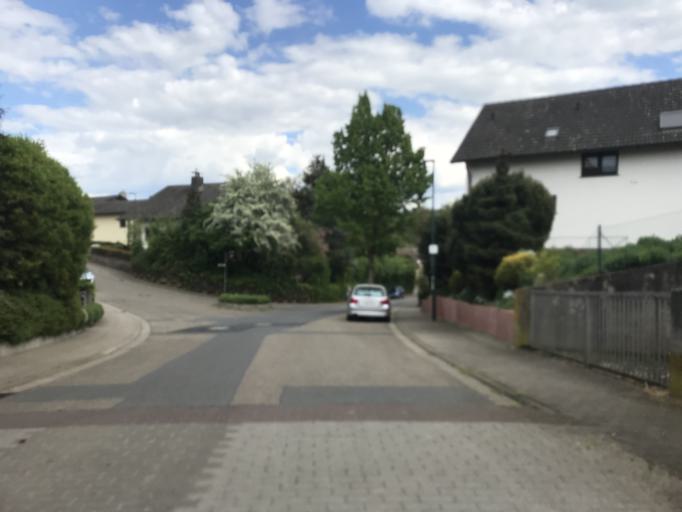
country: DE
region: Rheinland-Pfalz
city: Nackenheim
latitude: 49.9113
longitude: 8.3372
